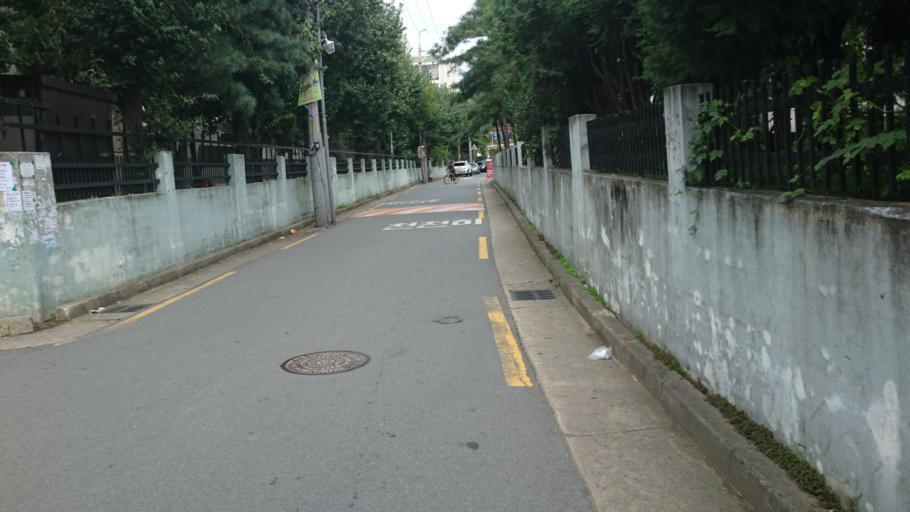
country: KR
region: Daegu
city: Daegu
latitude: 35.8776
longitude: 128.6687
